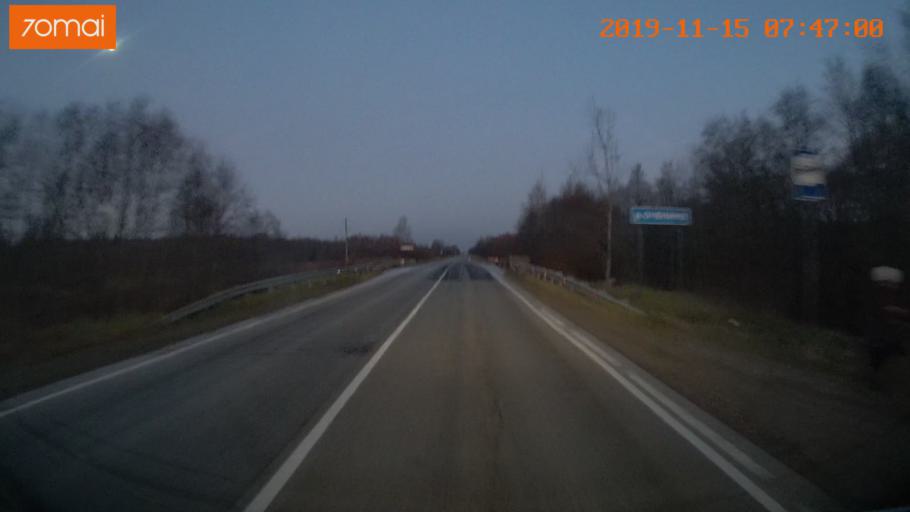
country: RU
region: Vologda
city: Sheksna
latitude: 58.8375
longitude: 38.2688
